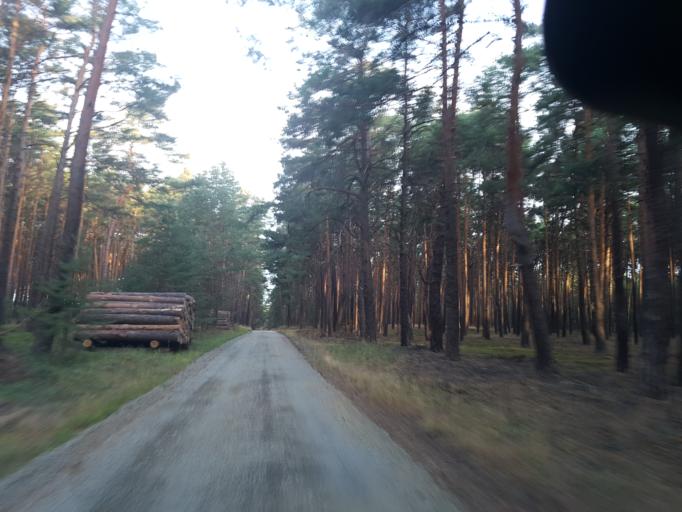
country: DE
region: Brandenburg
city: Schonewalde
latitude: 51.7467
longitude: 13.5592
